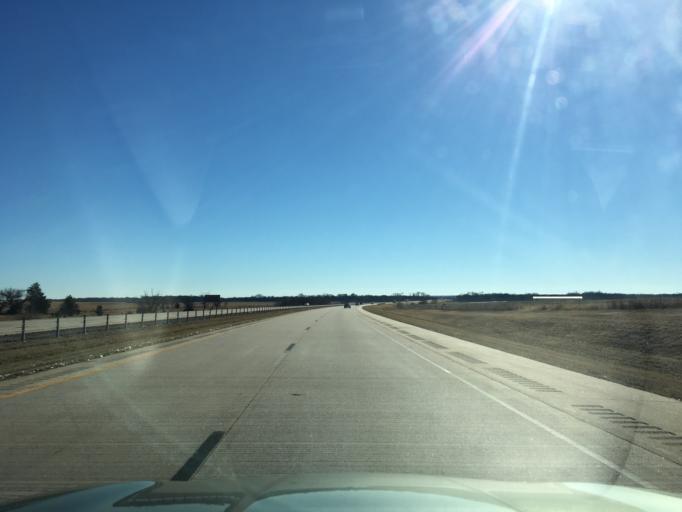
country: US
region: Oklahoma
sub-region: Kay County
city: Tonkawa
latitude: 36.4897
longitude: -97.3293
